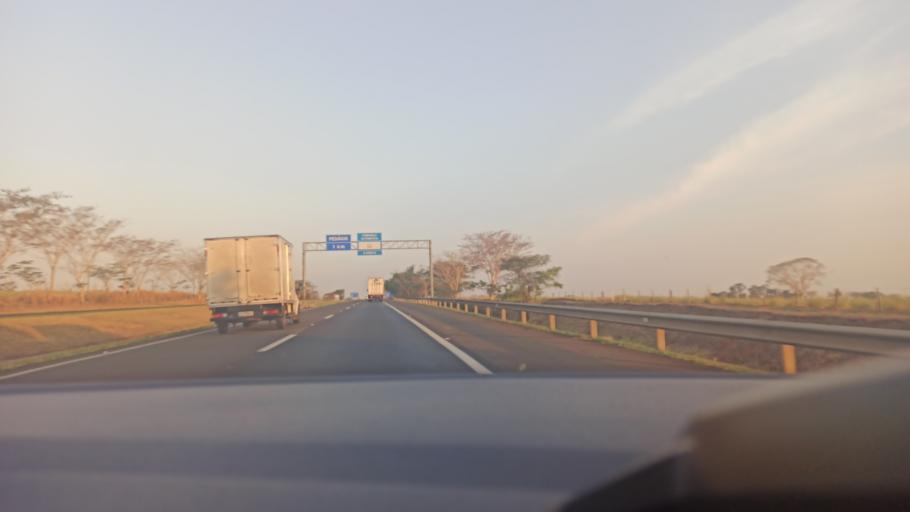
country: BR
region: Sao Paulo
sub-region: Santa Adelia
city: Santa Adelia
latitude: -21.3775
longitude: -48.7403
